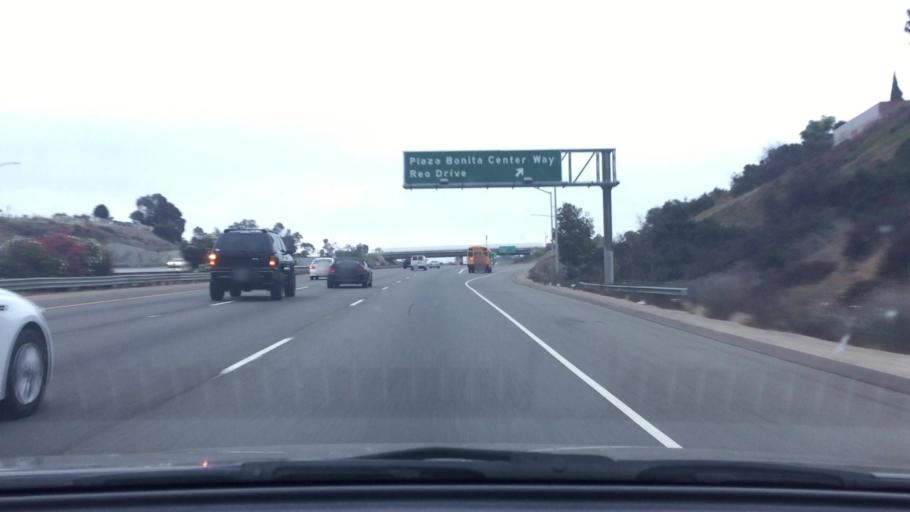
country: US
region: California
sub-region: San Diego County
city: Chula Vista
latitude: 32.6631
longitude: -117.0621
